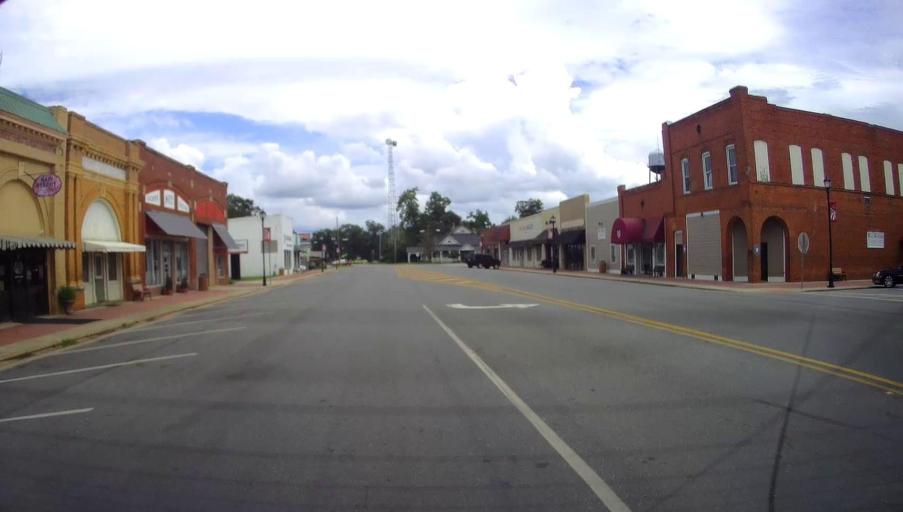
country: US
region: Georgia
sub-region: Schley County
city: Ellaville
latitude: 32.2382
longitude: -84.3085
